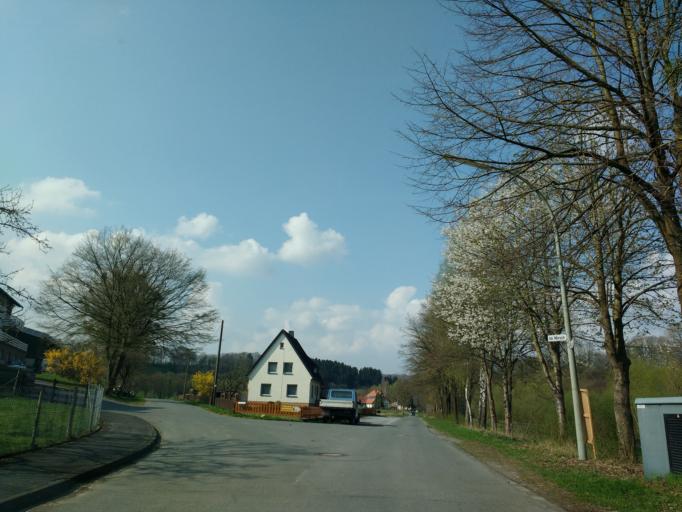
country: DE
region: North Rhine-Westphalia
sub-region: Regierungsbezirk Detmold
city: Paderborn
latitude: 51.6344
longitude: 8.7626
